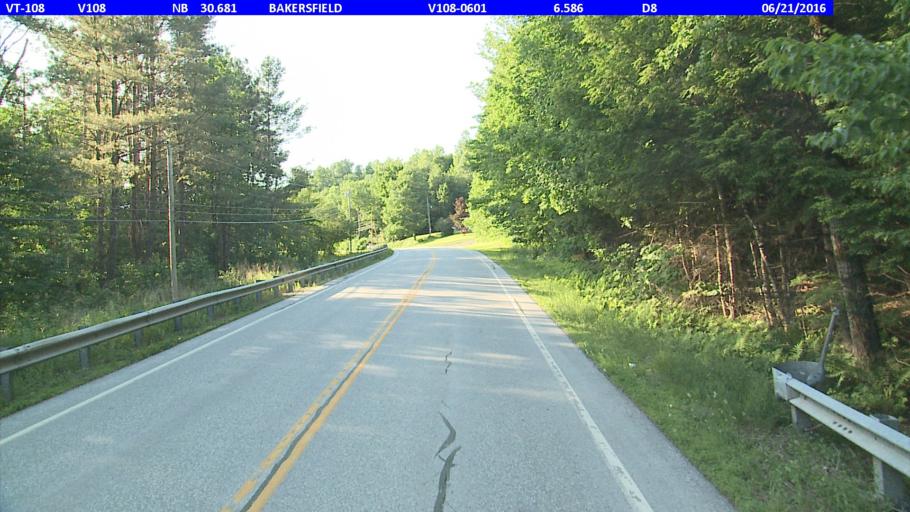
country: US
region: Vermont
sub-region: Franklin County
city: Enosburg Falls
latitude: 44.8210
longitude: -72.7924
